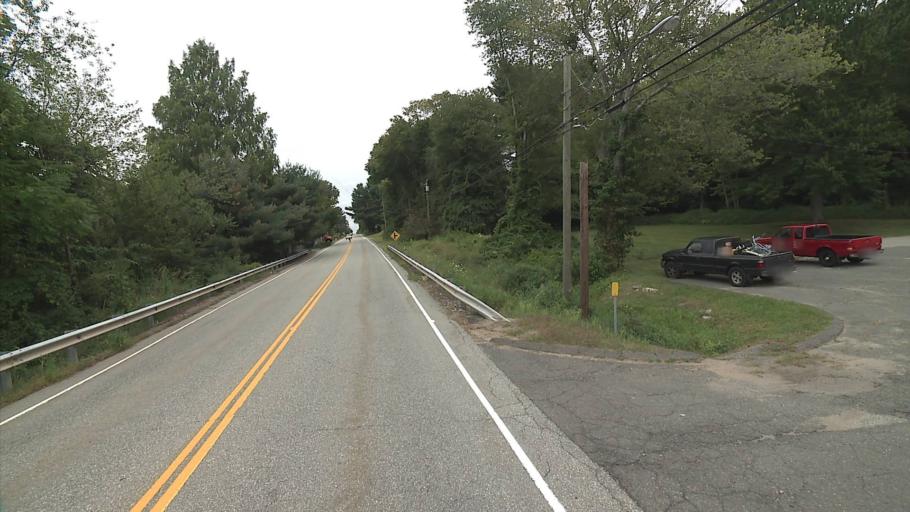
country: US
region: Connecticut
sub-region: Hartford County
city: Terramuggus
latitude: 41.7030
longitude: -72.4346
